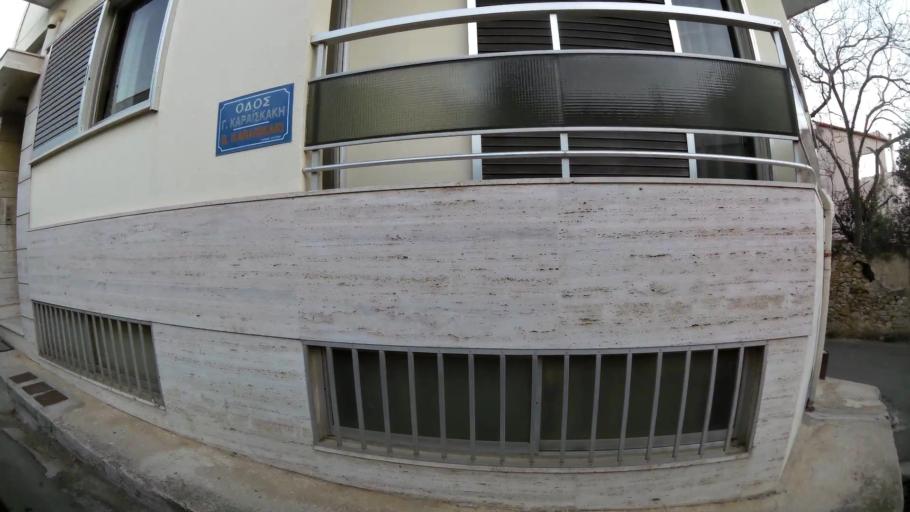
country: GR
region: Attica
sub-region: Nomarchia Anatolikis Attikis
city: Spata
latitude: 37.9631
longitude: 23.9133
